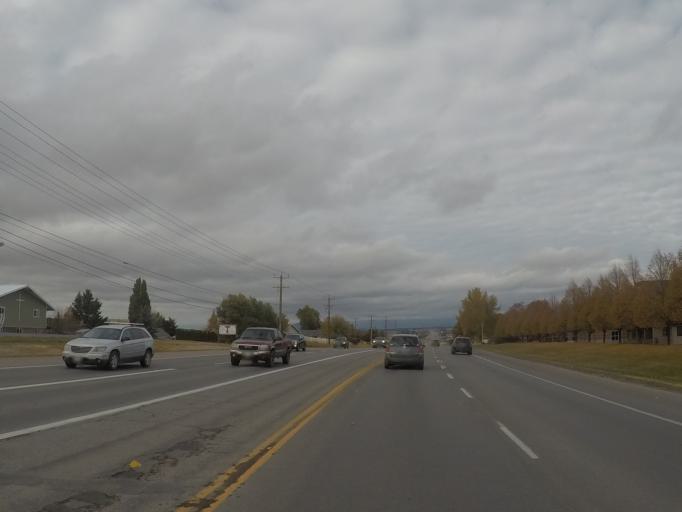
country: US
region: Montana
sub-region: Flathead County
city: Kalispell
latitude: 48.2202
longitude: -114.3305
